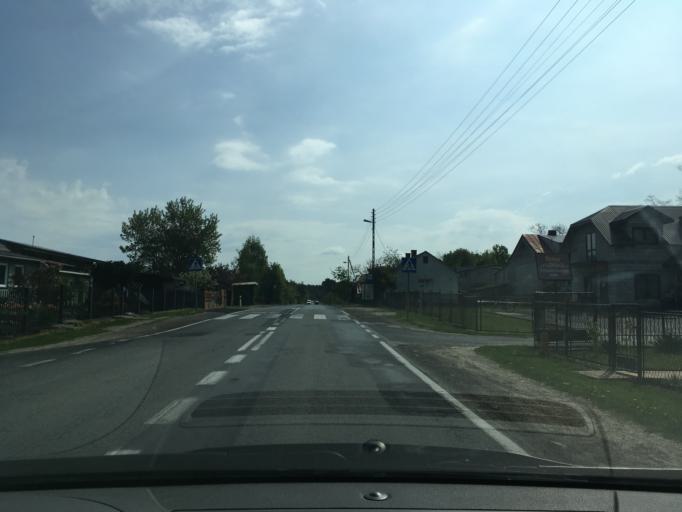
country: PL
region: Lublin Voivodeship
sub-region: Powiat pulawski
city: Pulawy
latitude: 51.4751
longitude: 21.9055
